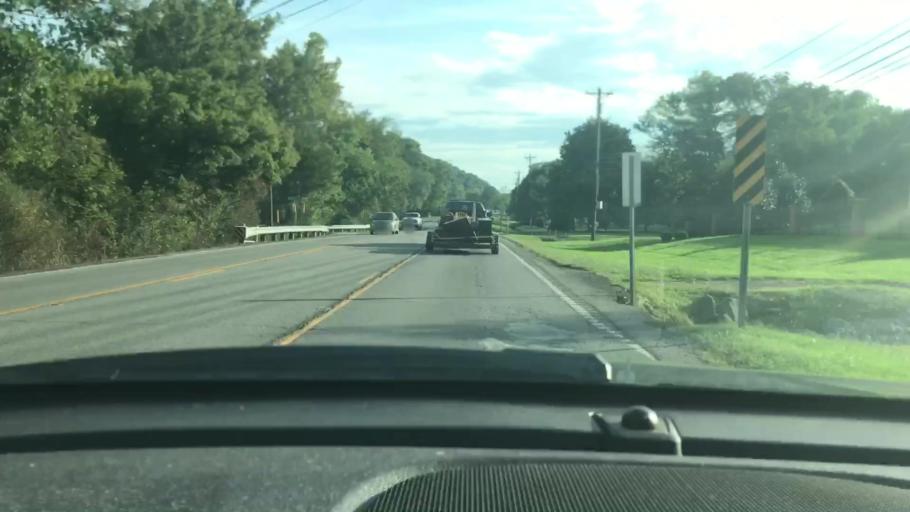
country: US
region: Tennessee
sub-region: Sumner County
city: Millersville
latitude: 36.3601
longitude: -86.7126
